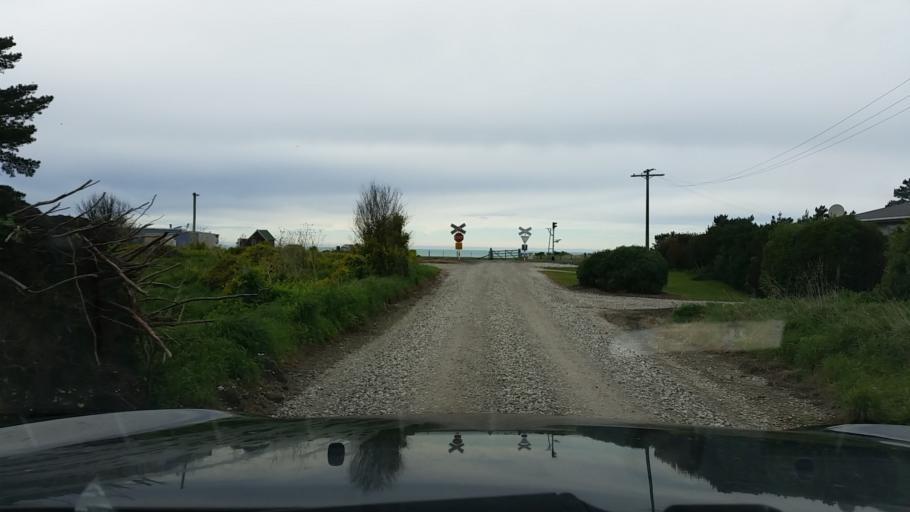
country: NZ
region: Marlborough
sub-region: Marlborough District
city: Blenheim
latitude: -41.9240
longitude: 174.0928
